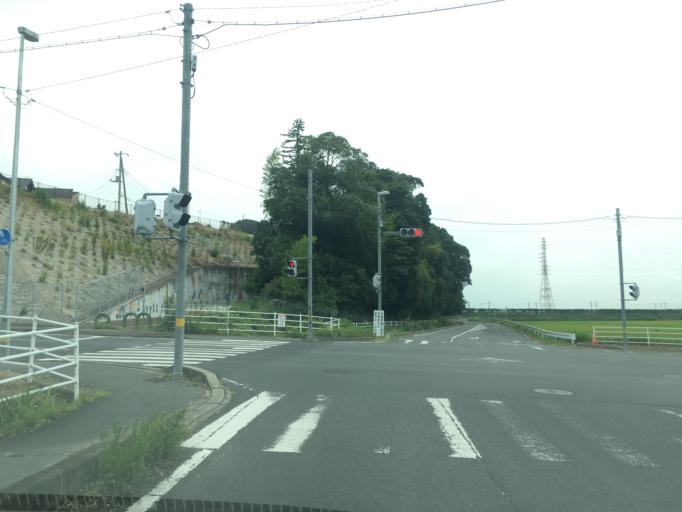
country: JP
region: Ibaraki
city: Katsuta
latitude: 36.3839
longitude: 140.5156
